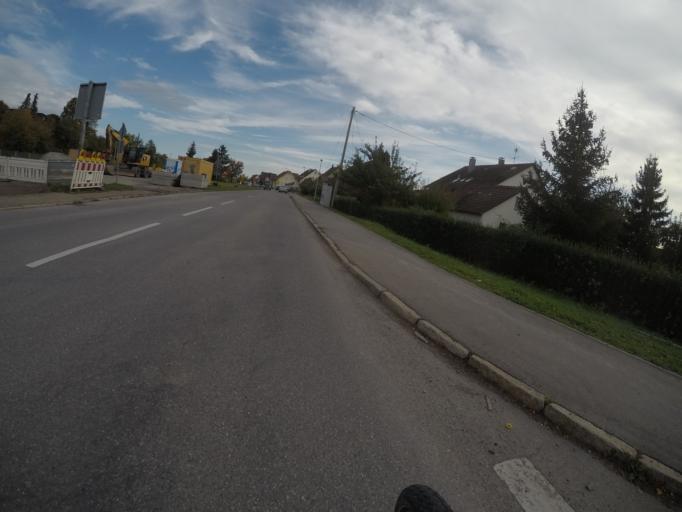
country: DE
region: Baden-Wuerttemberg
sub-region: Regierungsbezirk Stuttgart
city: Herrenberg
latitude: 48.5626
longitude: 8.9069
